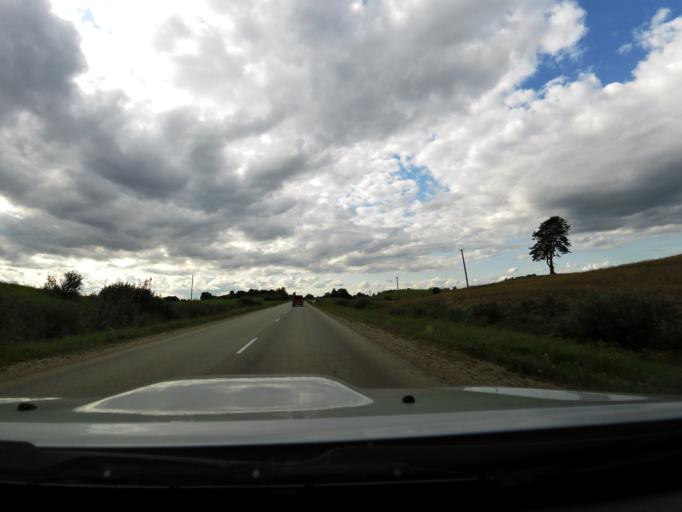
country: LV
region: Ilukste
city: Ilukste
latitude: 55.9745
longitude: 26.0199
